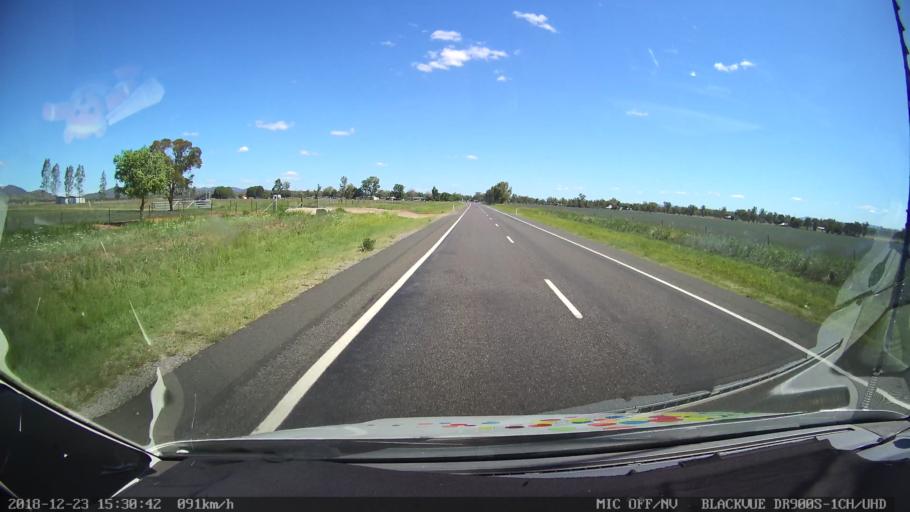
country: AU
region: New South Wales
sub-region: Tamworth Municipality
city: East Tamworth
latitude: -30.9624
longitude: 150.8663
